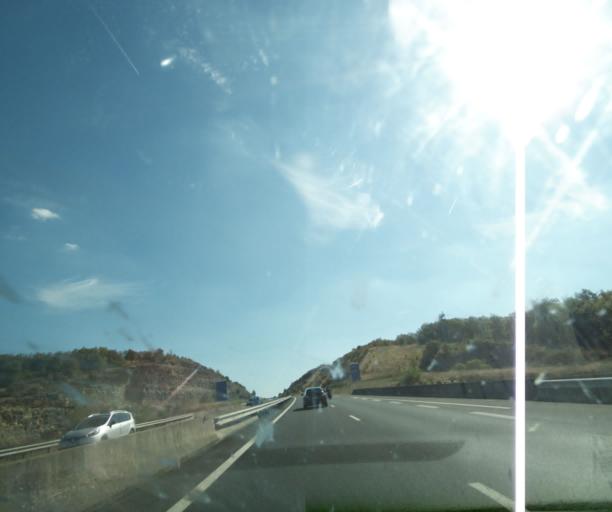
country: FR
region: Limousin
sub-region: Departement de la Correze
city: Brive-la-Gaillarde
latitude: 45.0597
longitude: 1.5068
